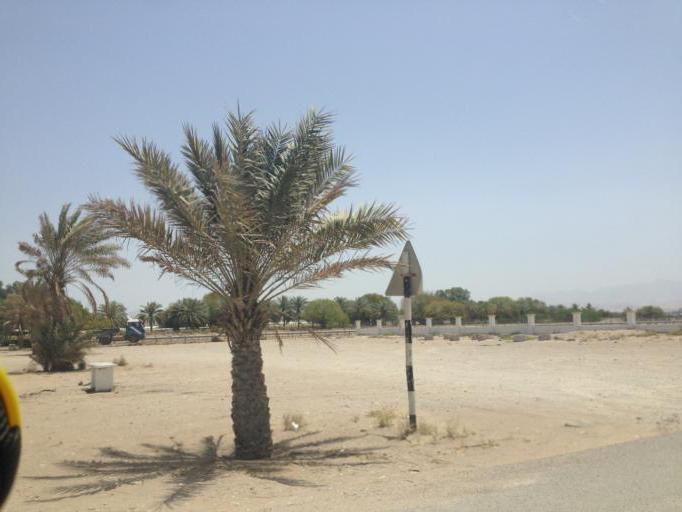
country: OM
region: Muhafazat Masqat
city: As Sib al Jadidah
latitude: 23.6308
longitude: 58.2609
